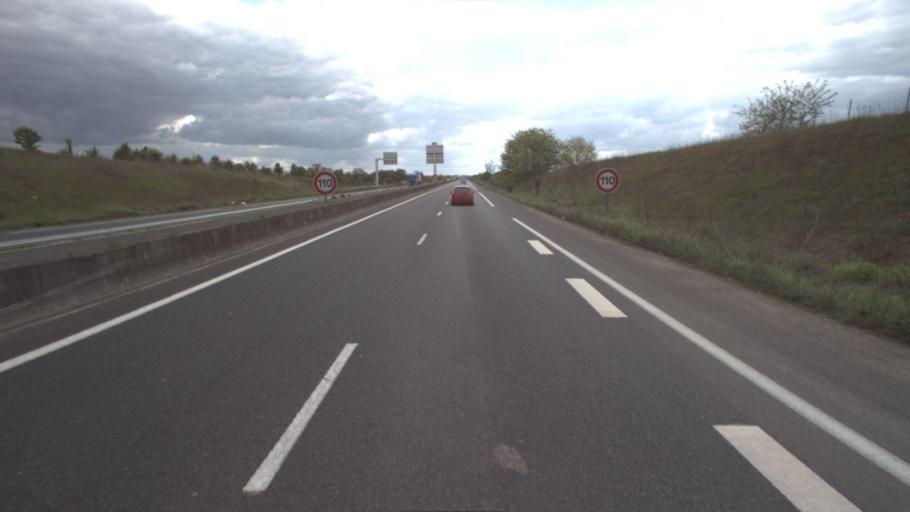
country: FR
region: Ile-de-France
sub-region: Departement de Seine-et-Marne
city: Villenoy
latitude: 48.9376
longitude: 2.8467
